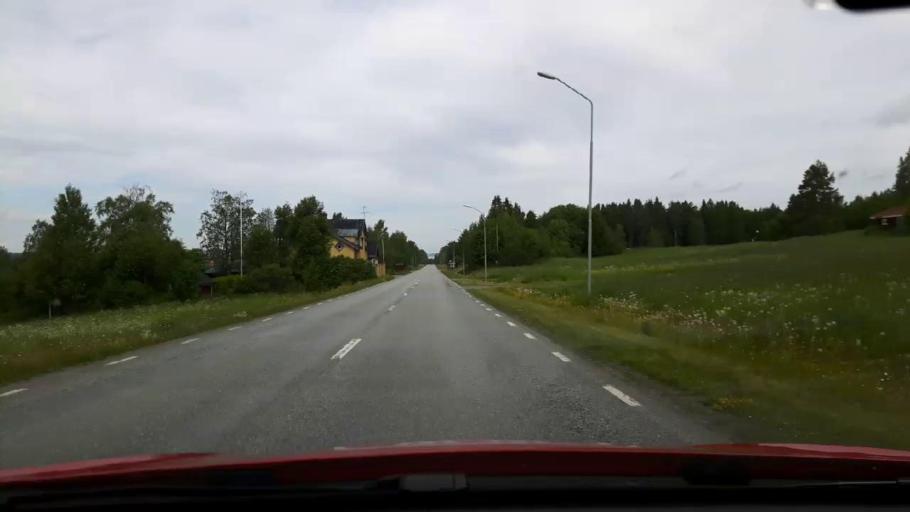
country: SE
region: Jaemtland
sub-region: Bergs Kommun
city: Hoverberg
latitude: 62.9685
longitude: 14.4880
